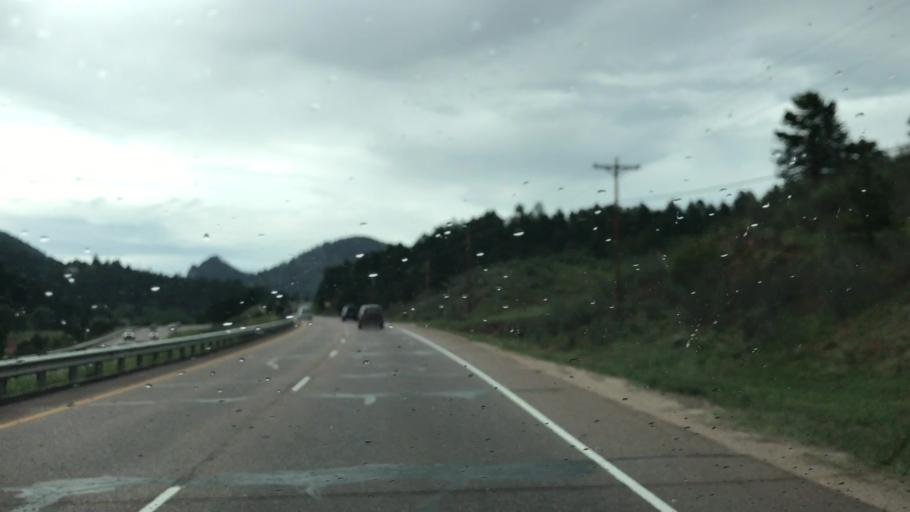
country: US
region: Colorado
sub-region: El Paso County
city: Cascade-Chipita Park
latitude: 38.9469
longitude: -105.0216
